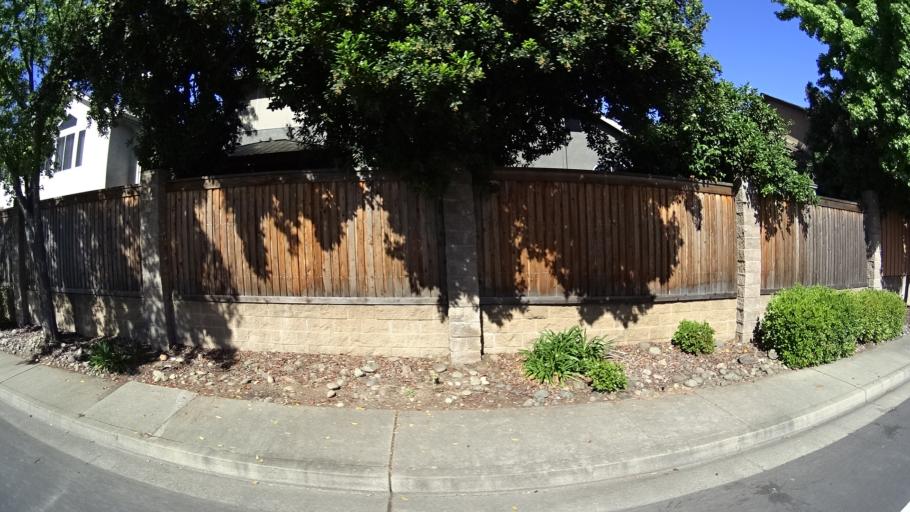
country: US
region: California
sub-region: Placer County
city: Rocklin
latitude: 38.7899
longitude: -121.2636
